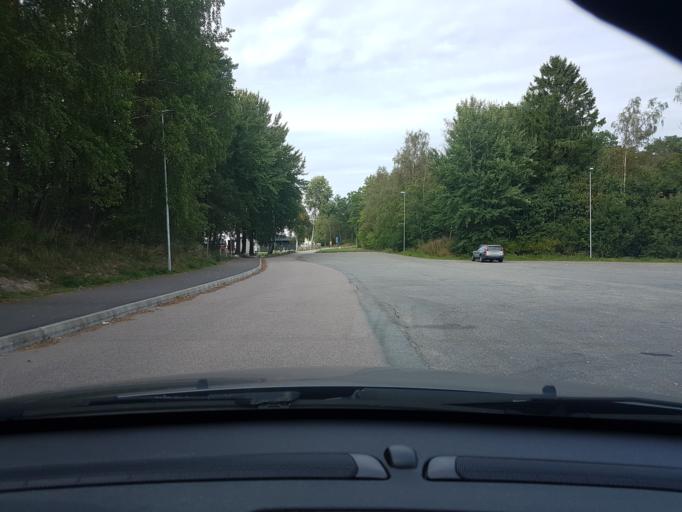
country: SE
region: Vaestra Goetaland
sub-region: Ale Kommun
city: Surte
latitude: 57.8527
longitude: 12.0386
